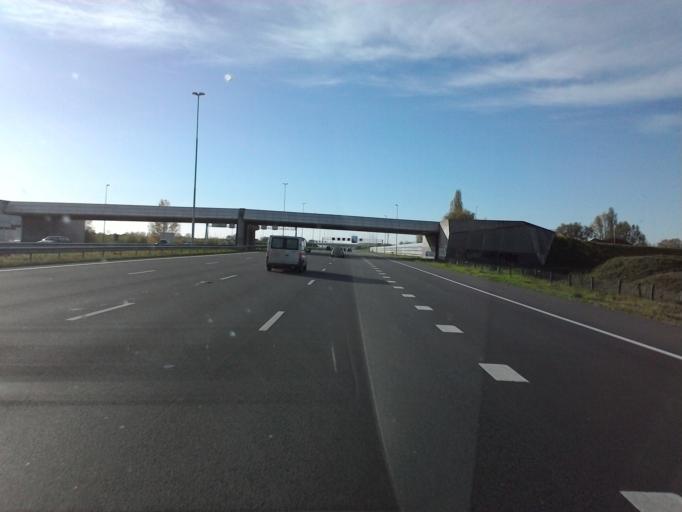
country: NL
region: Gelderland
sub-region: Gemeente Culemborg
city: Culemborg
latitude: 51.9371
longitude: 5.1555
